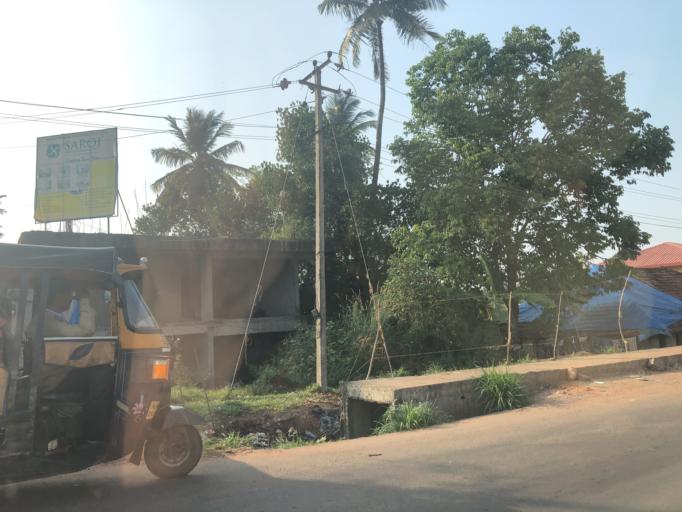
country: IN
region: Karnataka
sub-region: Dakshina Kannada
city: Ullal
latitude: 12.8146
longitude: 74.8585
